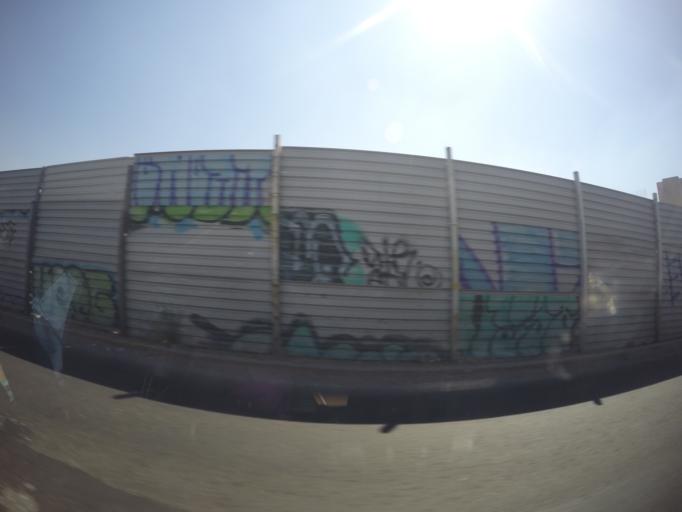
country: MX
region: Mexico
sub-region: Atenco
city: Colonia el Salado
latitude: 19.5864
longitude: -99.0253
